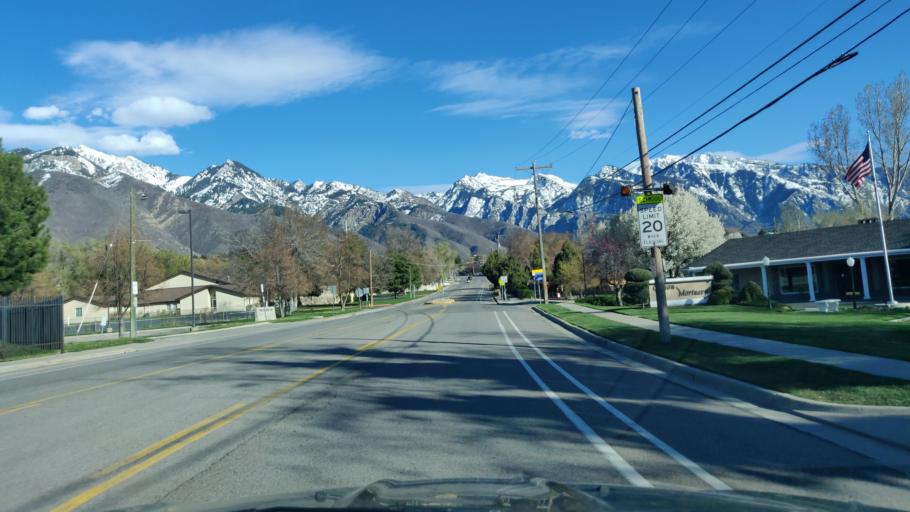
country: US
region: Utah
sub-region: Salt Lake County
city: Little Cottonwood Creek Valley
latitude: 40.6126
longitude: -111.8211
